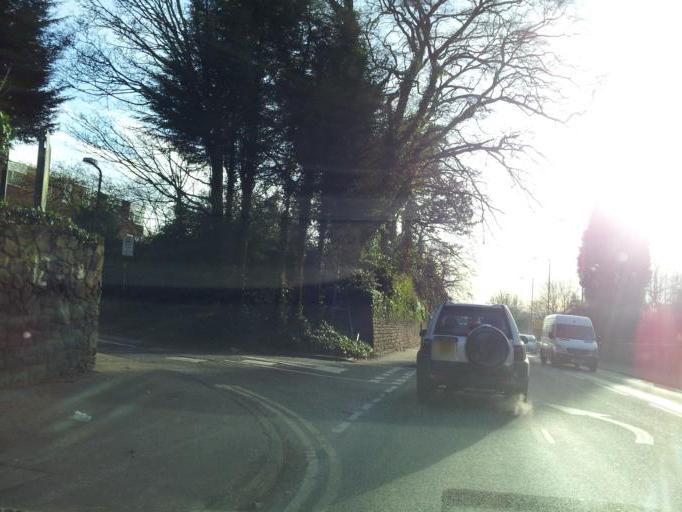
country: GB
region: England
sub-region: City and Borough of Birmingham
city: Birmingham
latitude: 52.5156
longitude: -1.8497
